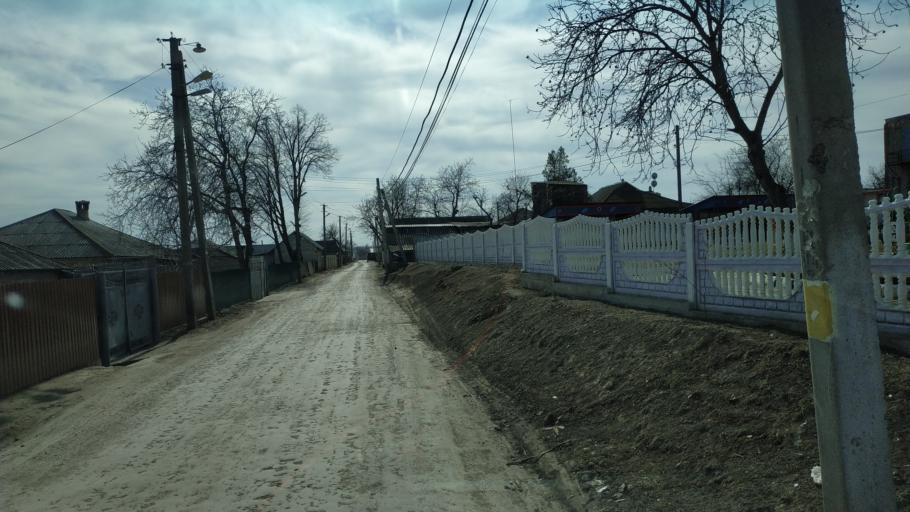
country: MD
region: Nisporeni
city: Nisporeni
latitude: 46.9626
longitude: 28.2108
